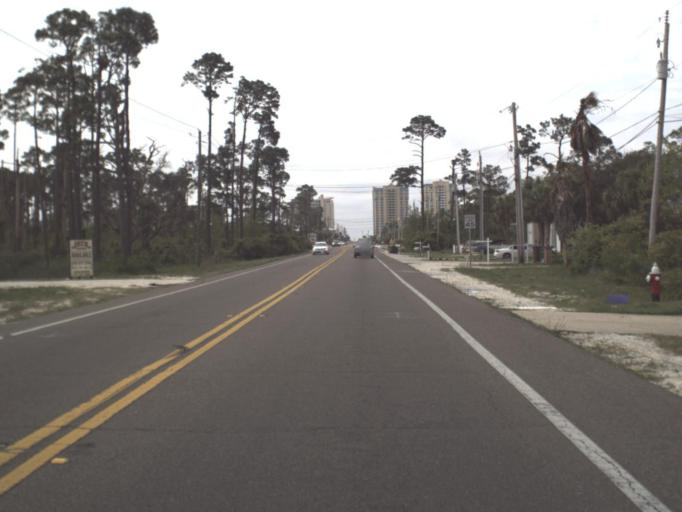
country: US
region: Alabama
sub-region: Baldwin County
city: Orange Beach
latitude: 30.3071
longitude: -87.4275
